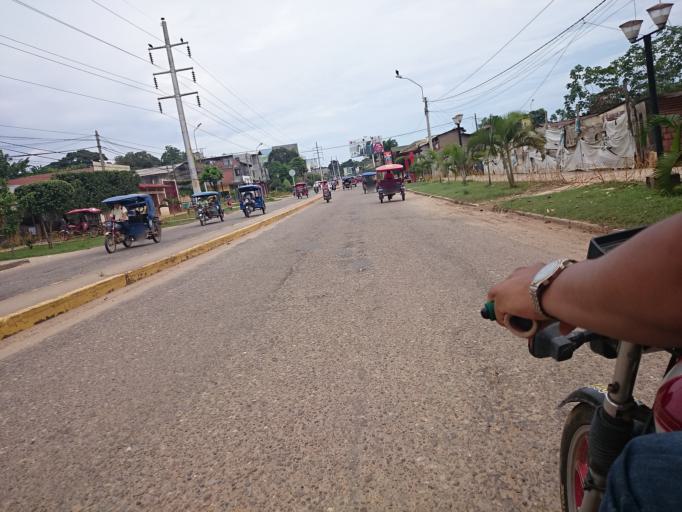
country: PE
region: Ucayali
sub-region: Provincia de Coronel Portillo
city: Pucallpa
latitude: -8.3683
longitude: -74.5622
